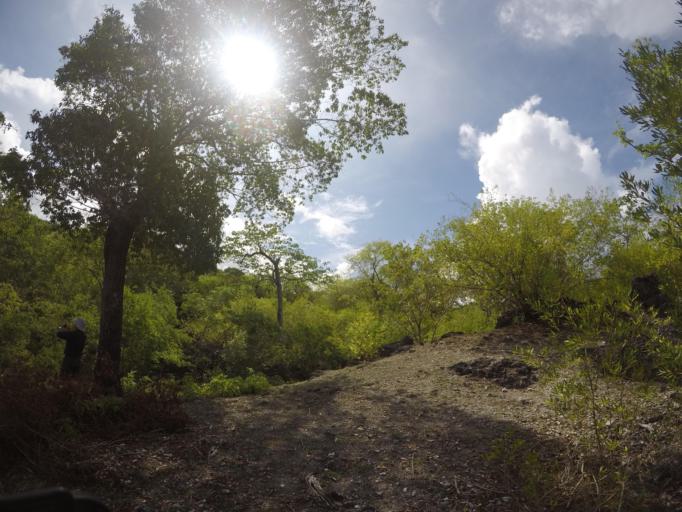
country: TL
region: Lautem
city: Lospalos
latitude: -8.3455
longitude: 127.0484
